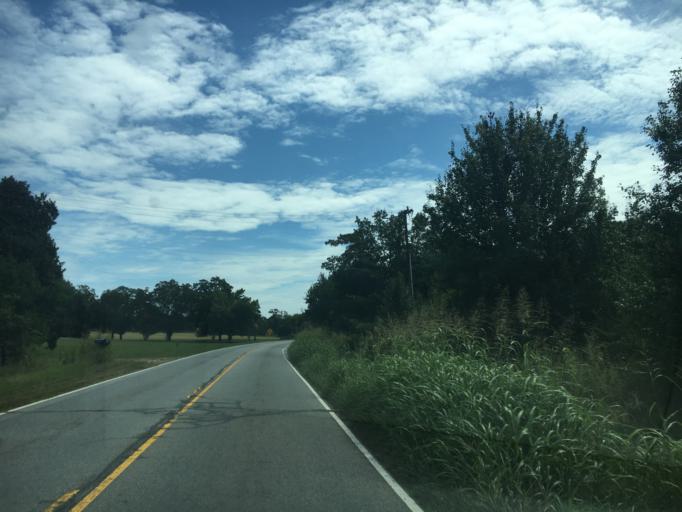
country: US
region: South Carolina
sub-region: Greenville County
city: Fountain Inn
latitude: 34.6352
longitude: -82.1369
